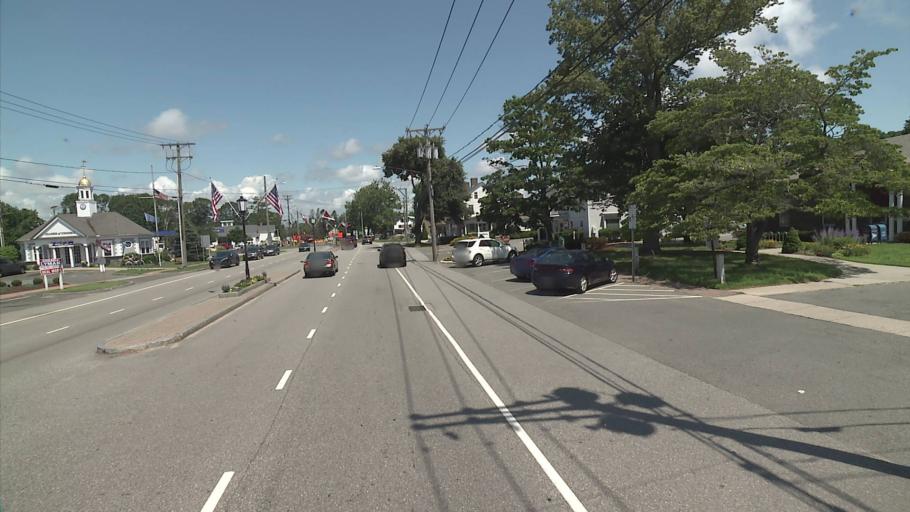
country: US
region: Connecticut
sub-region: Middlesex County
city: Old Saybrook
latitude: 41.2963
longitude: -72.3768
